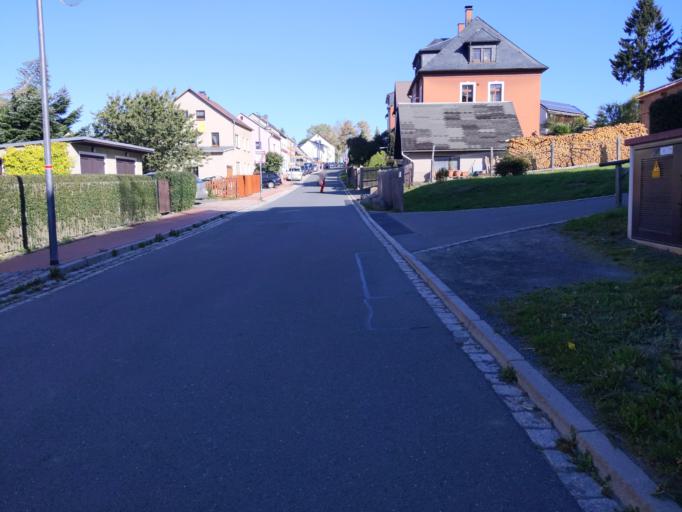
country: DE
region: Saxony
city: Pohl
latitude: 50.3938
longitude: 12.3281
